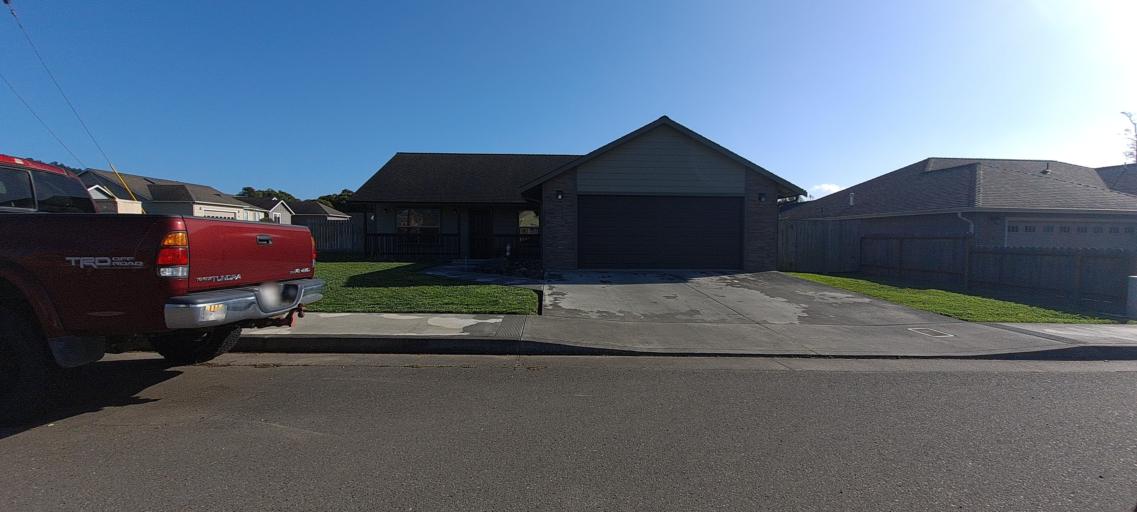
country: US
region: California
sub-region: Humboldt County
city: Fortuna
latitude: 40.5739
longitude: -124.1346
